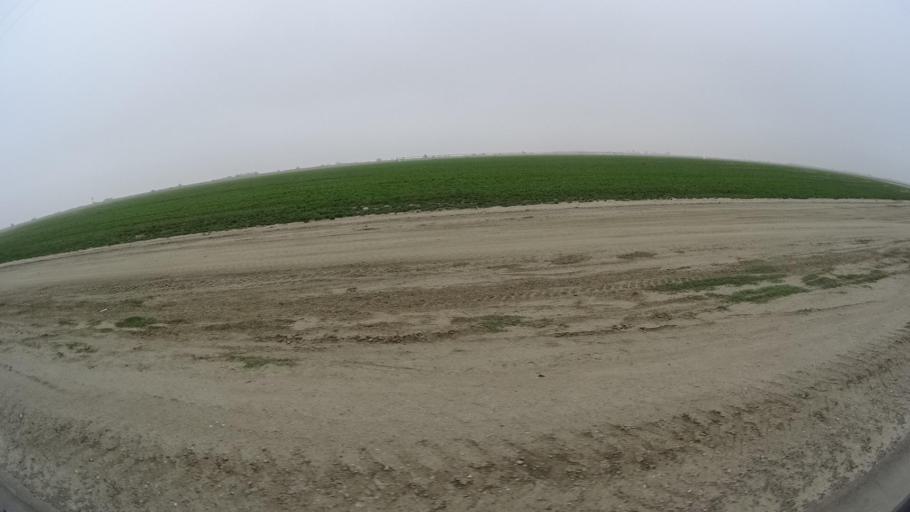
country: US
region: California
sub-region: Kern County
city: Rosedale
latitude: 35.2206
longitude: -119.2329
